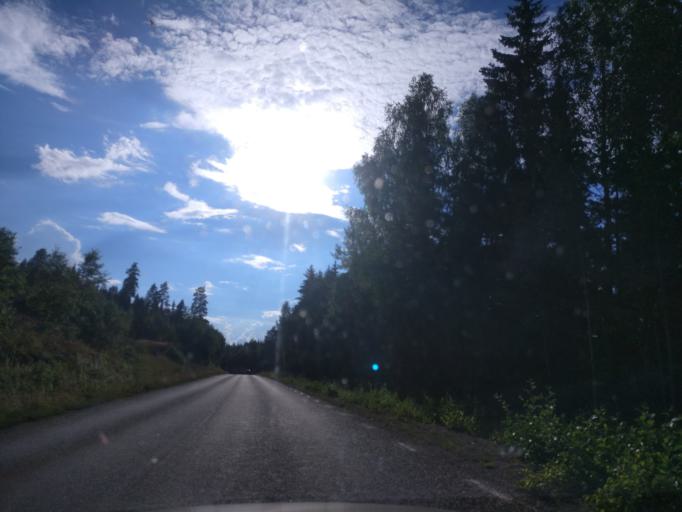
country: SE
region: Dalarna
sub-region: Ludvika Kommun
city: Ludvika
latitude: 60.2924
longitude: 15.1245
